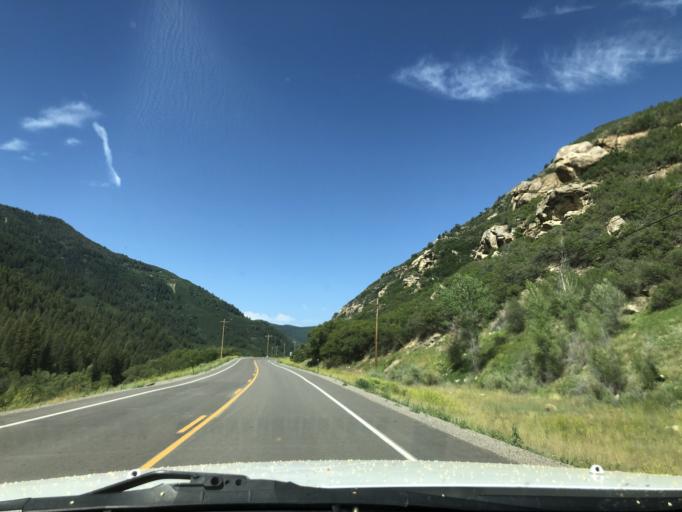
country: US
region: Colorado
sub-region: Delta County
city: Paonia
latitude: 38.9367
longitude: -107.3898
